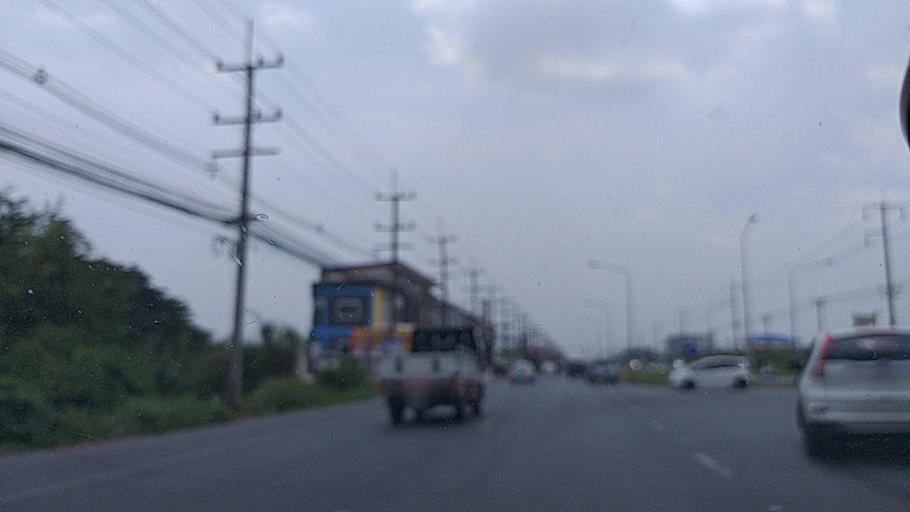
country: TH
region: Nakhon Pathom
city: Salaya
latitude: 13.7782
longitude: 100.3025
